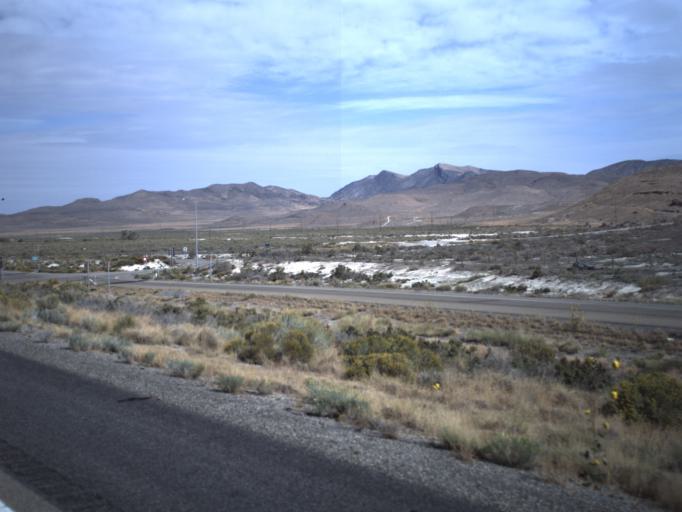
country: US
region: Utah
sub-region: Tooele County
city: Grantsville
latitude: 40.7621
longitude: -112.7798
